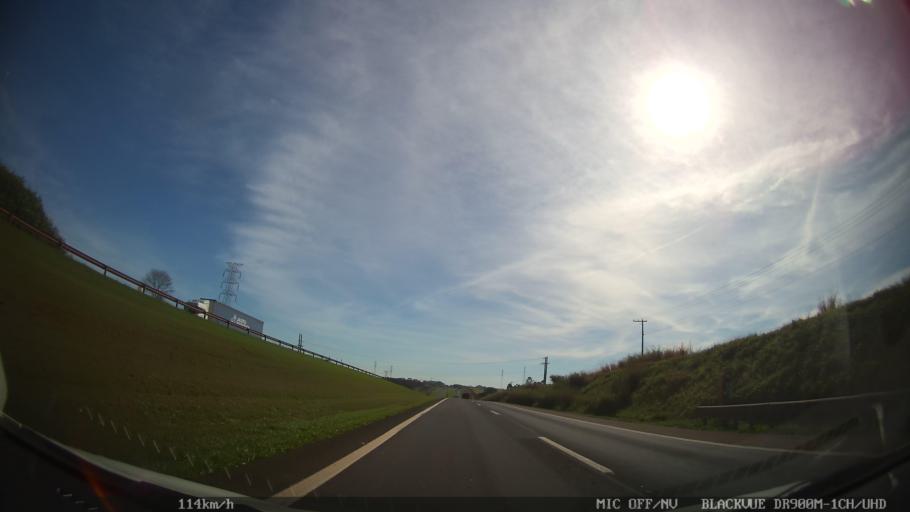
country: BR
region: Sao Paulo
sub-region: Araras
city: Araras
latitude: -22.2978
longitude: -47.3923
